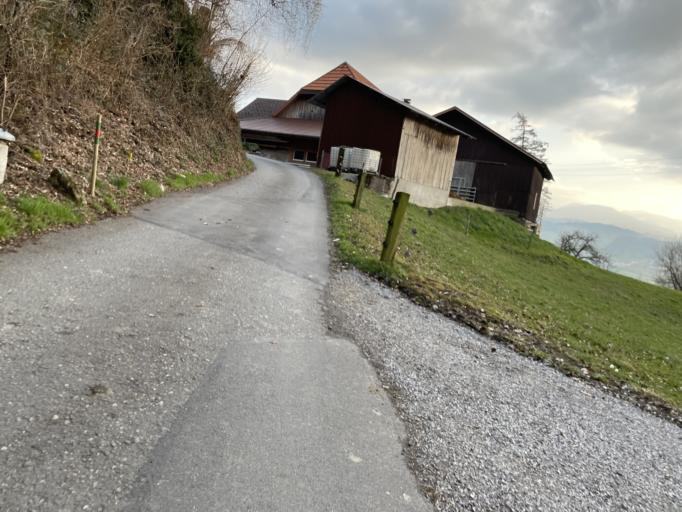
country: CH
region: Bern
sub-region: Bern-Mittelland District
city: Toffen
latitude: 46.8444
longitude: 7.5203
